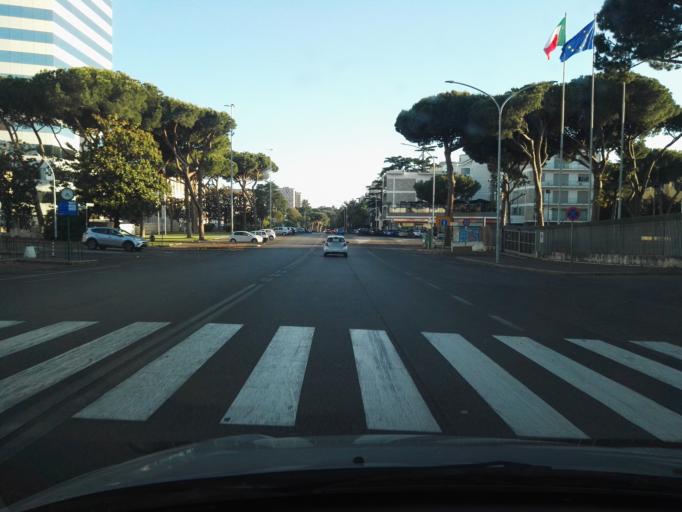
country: IT
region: Latium
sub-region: Citta metropolitana di Roma Capitale
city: Selcetta
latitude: 41.8314
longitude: 12.4753
